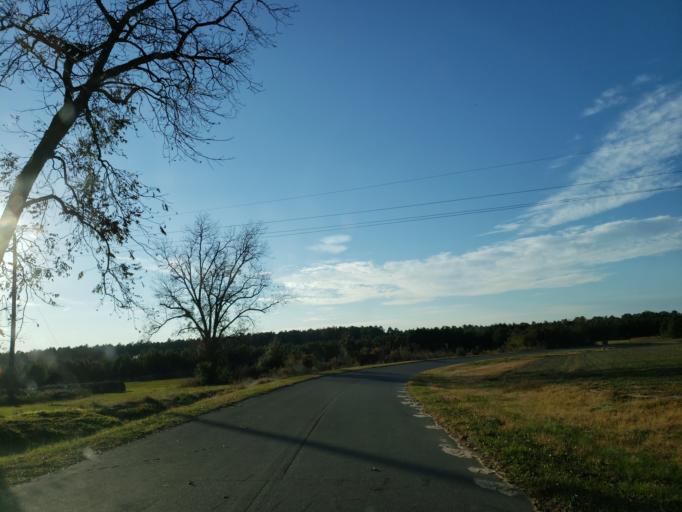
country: US
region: Georgia
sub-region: Dooly County
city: Unadilla
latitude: 32.1988
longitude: -83.7642
